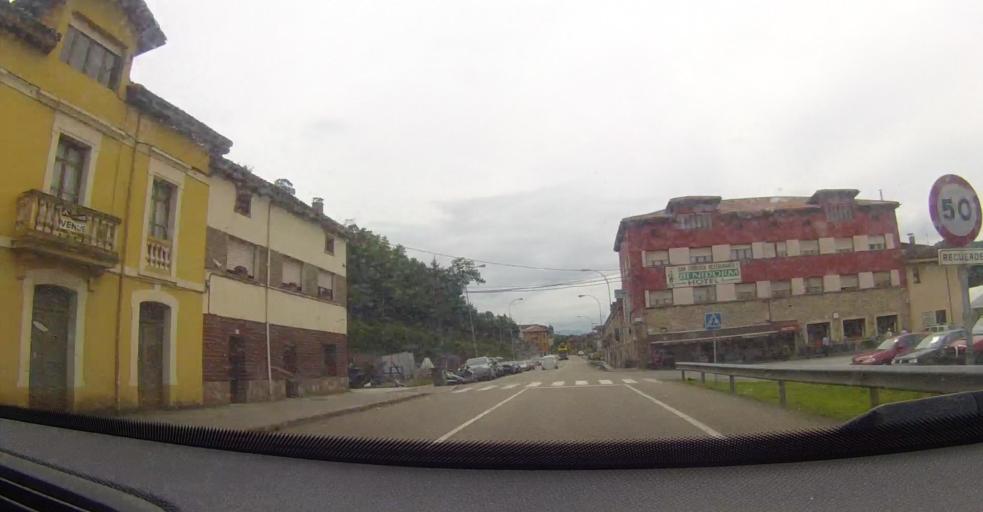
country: ES
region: Asturias
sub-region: Province of Asturias
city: Pilona
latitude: 43.3616
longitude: -5.3023
